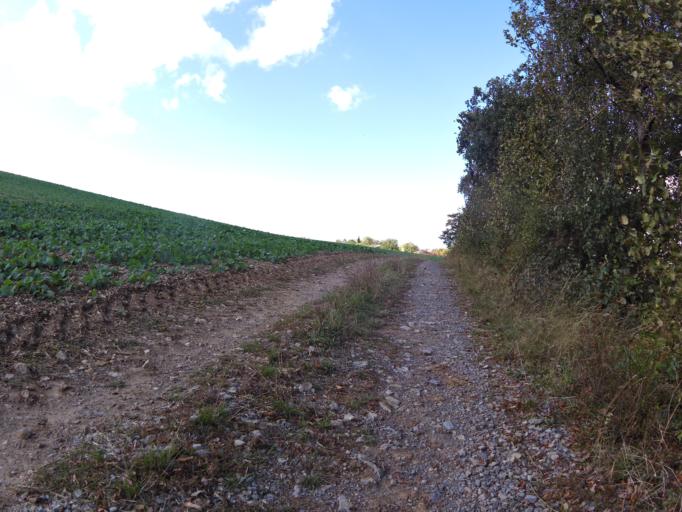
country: DE
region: Bavaria
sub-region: Regierungsbezirk Unterfranken
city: Erlabrunn
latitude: 49.8384
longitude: 9.8324
